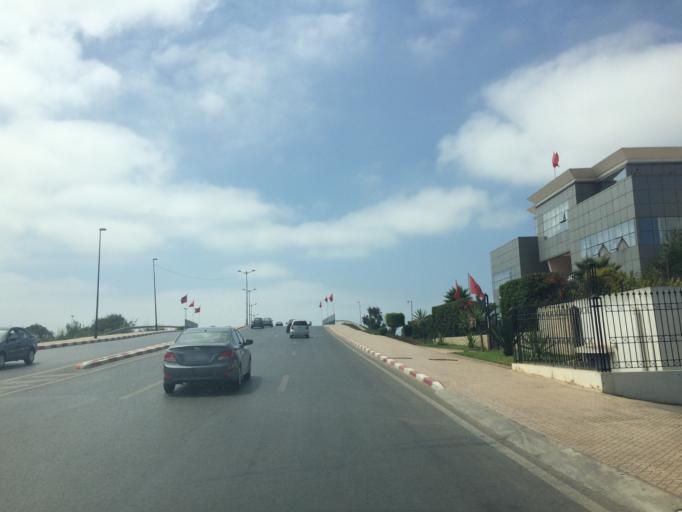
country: MA
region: Rabat-Sale-Zemmour-Zaer
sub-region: Skhirate-Temara
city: Temara
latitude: 33.9711
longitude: -6.8776
